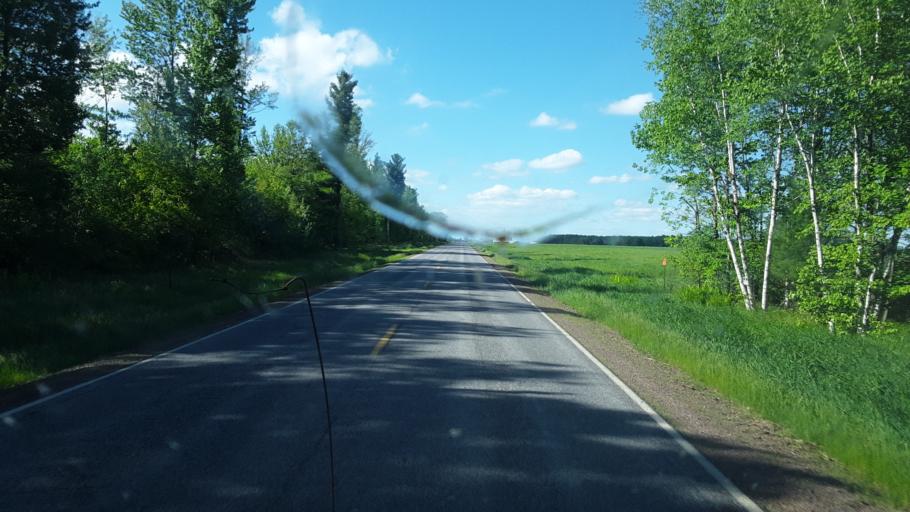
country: US
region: Wisconsin
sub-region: Wood County
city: Marshfield
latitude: 44.4126
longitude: -90.1601
